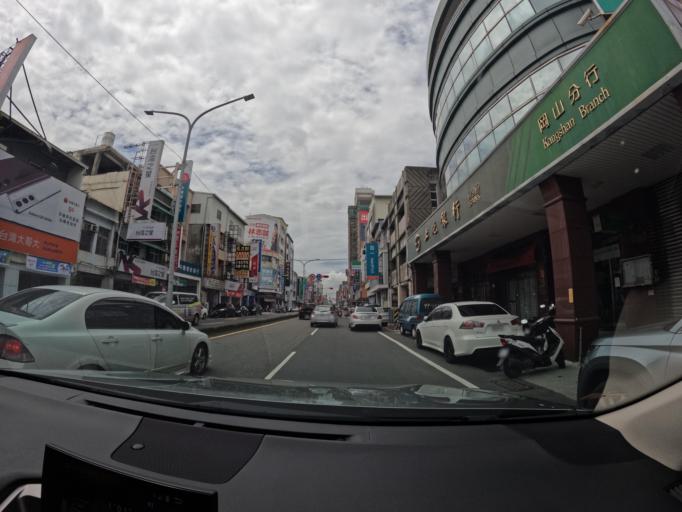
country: TW
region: Kaohsiung
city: Kaohsiung
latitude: 22.7950
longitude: 120.2957
